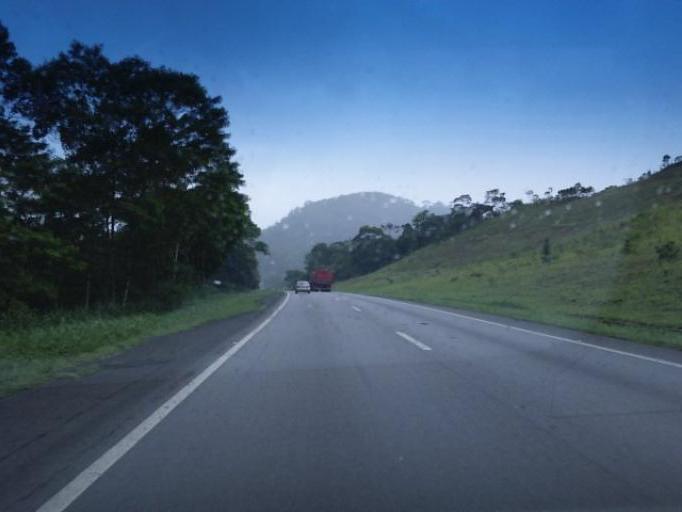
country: BR
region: Sao Paulo
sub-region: Cajati
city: Cajati
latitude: -24.8918
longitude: -48.2326
